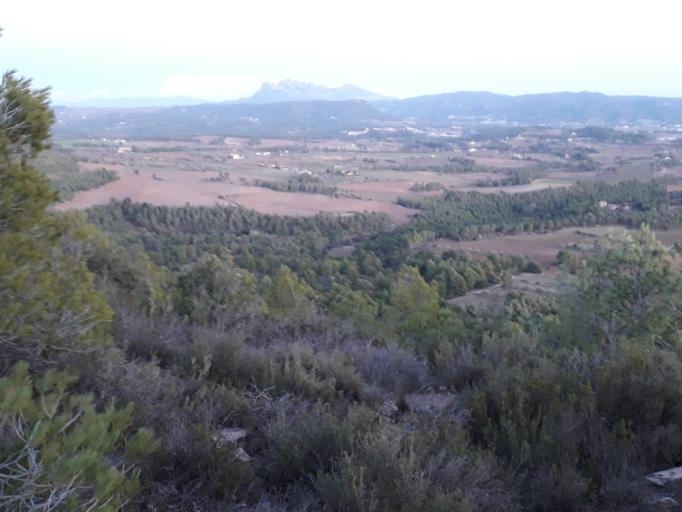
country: ES
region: Catalonia
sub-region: Provincia de Barcelona
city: Jorba
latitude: 41.6154
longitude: 1.5792
